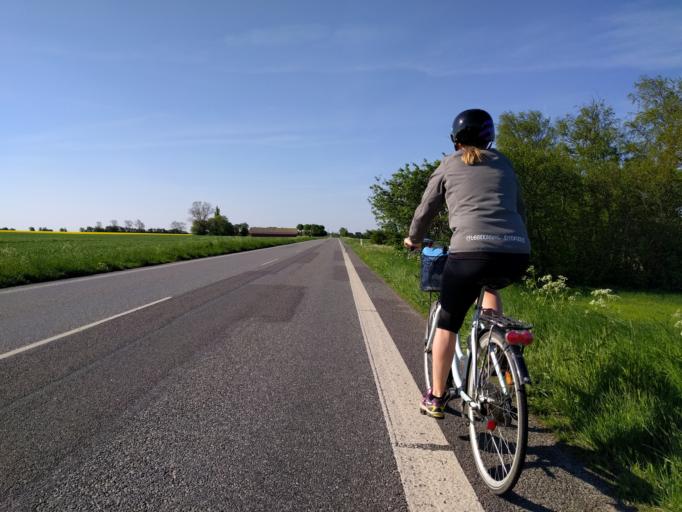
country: DK
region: Zealand
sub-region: Guldborgsund Kommune
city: Stubbekobing
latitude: 54.8163
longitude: 11.9932
